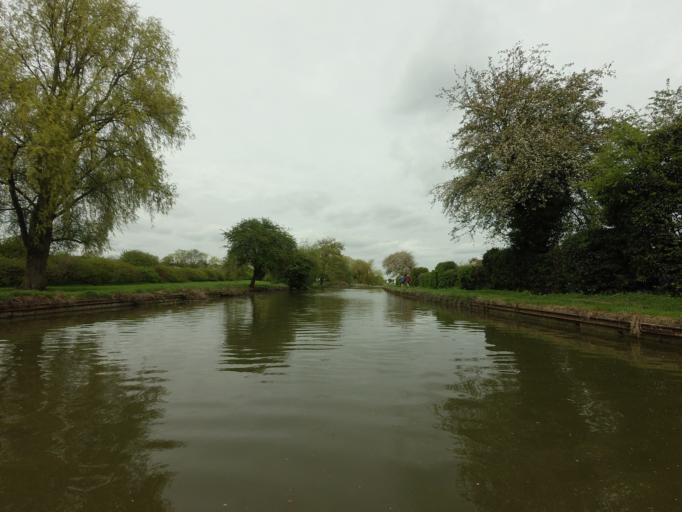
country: GB
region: England
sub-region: Milton Keynes
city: Milton Keynes
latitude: 52.0692
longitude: -0.7463
